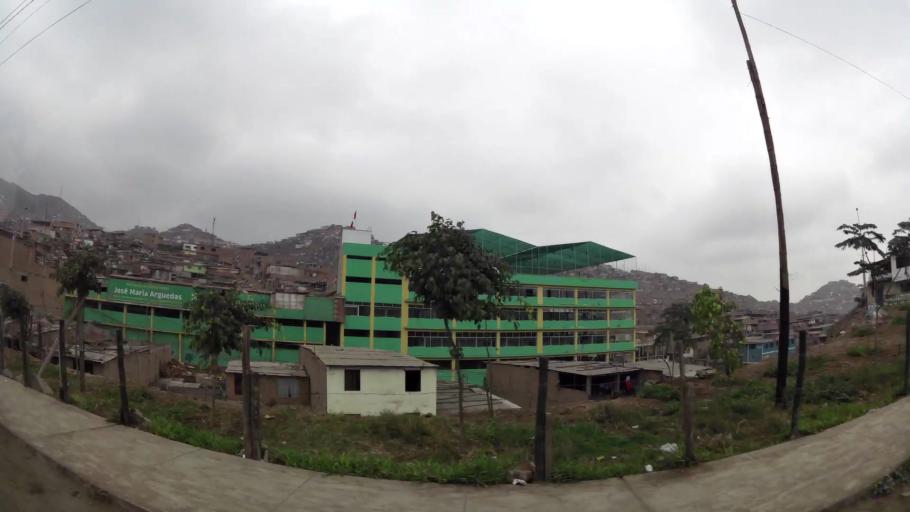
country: PE
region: Lima
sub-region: Lima
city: La Molina
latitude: -12.1316
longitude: -76.9556
